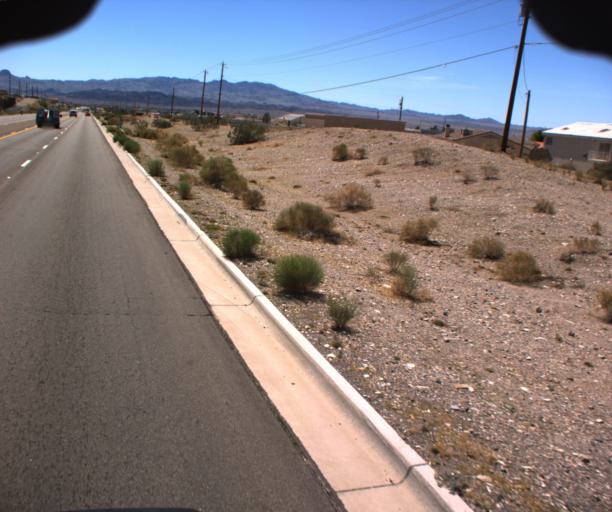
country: US
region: Arizona
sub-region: Mohave County
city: Lake Havasu City
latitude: 34.5112
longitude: -114.3496
